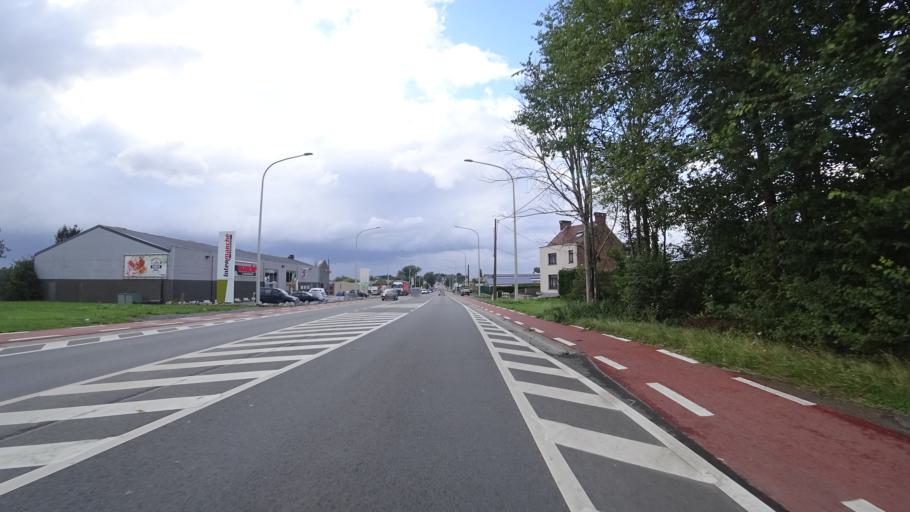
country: BE
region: Wallonia
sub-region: Province du Brabant Wallon
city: Chastre-Villeroux-Blanmont
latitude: 50.6382
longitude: 4.6498
